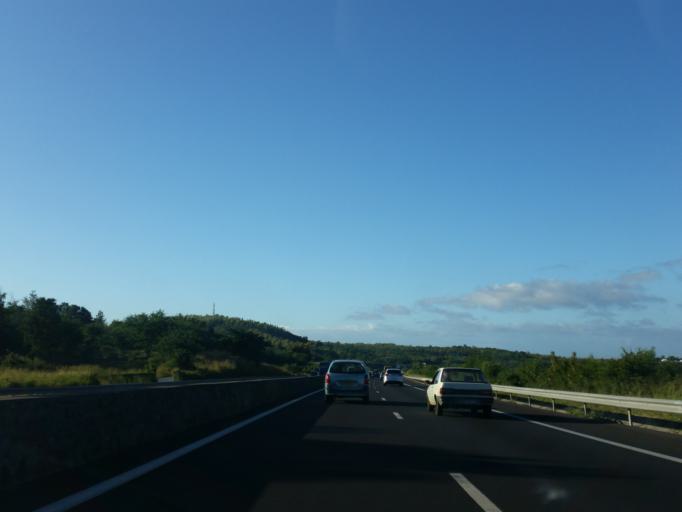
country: RE
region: Reunion
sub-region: Reunion
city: Les Avirons
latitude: -21.2570
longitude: 55.3328
